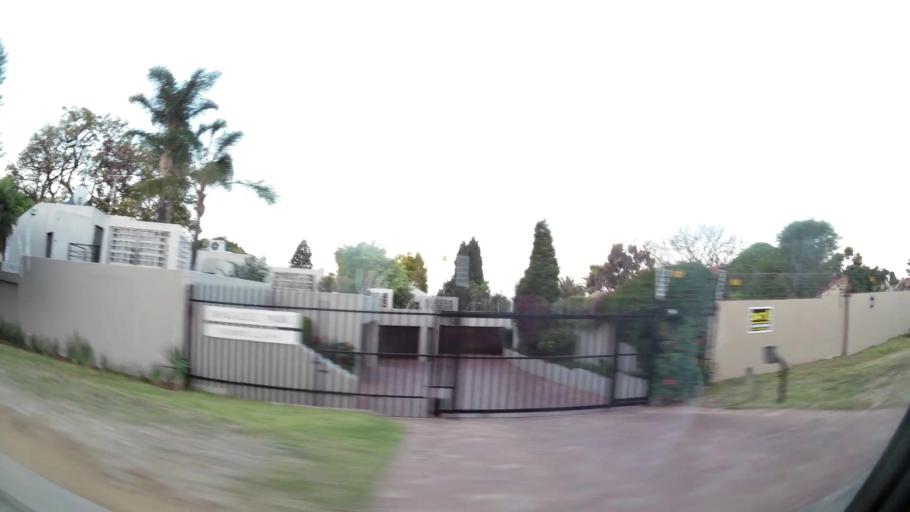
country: ZA
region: Gauteng
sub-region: City of Johannesburg Metropolitan Municipality
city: Diepsloot
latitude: -26.0308
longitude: 28.0235
